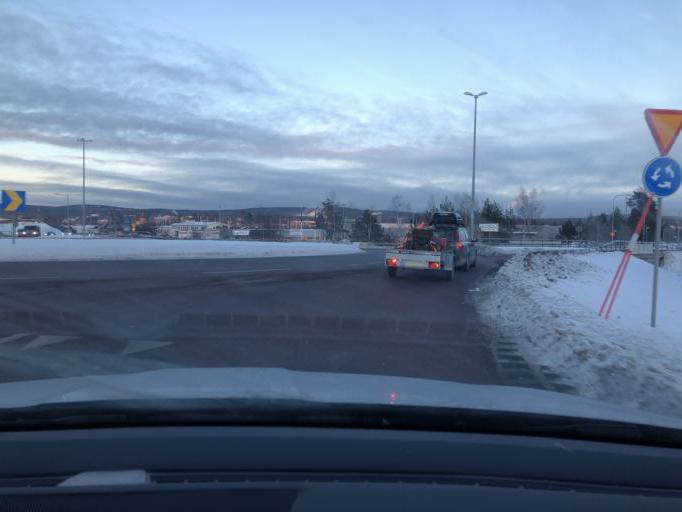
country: SE
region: Dalarna
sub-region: Faluns Kommun
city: Falun
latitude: 60.5953
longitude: 15.6199
